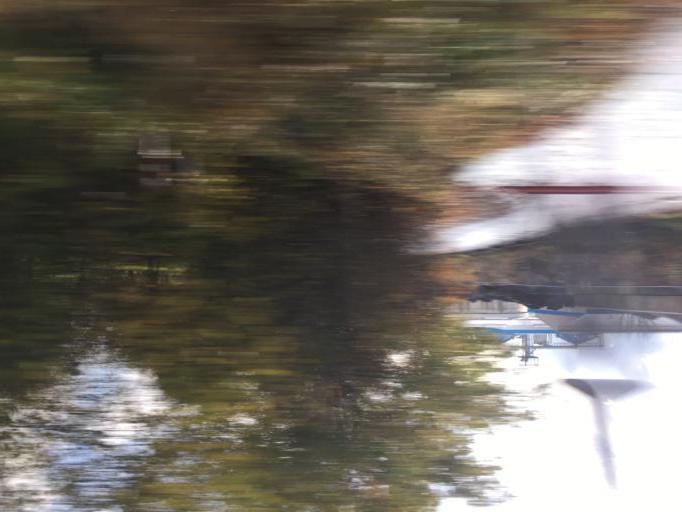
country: DE
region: North Rhine-Westphalia
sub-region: Regierungsbezirk Munster
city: Nordwalde
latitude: 52.0816
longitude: 7.4581
